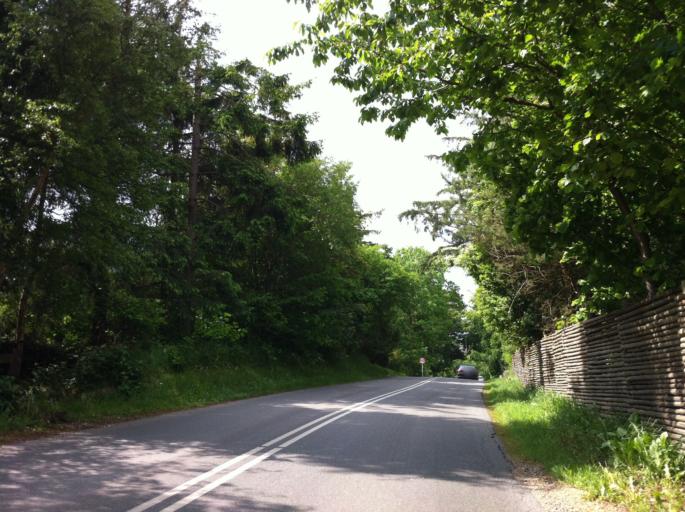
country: DK
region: Capital Region
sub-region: Gribskov Kommune
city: Helsinge
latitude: 56.1113
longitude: 12.2018
